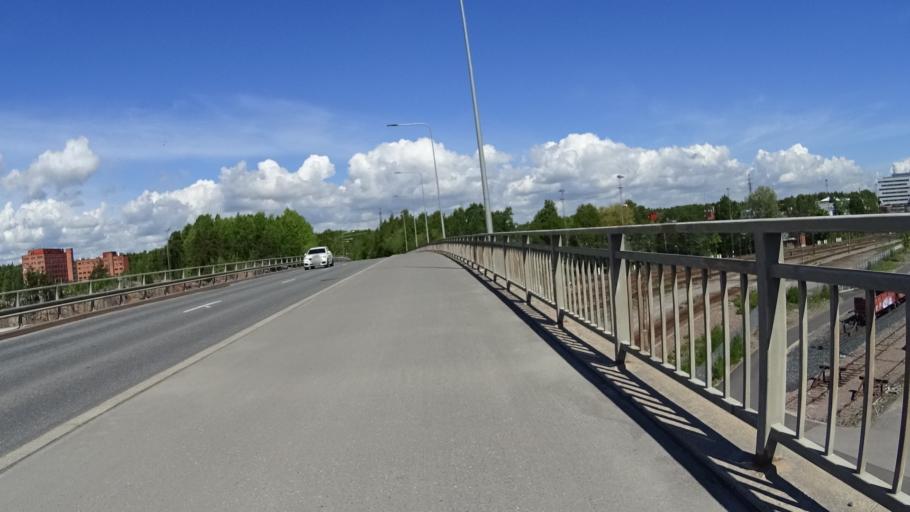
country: FI
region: Uusimaa
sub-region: Helsinki
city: Helsinki
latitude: 60.2169
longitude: 24.9341
